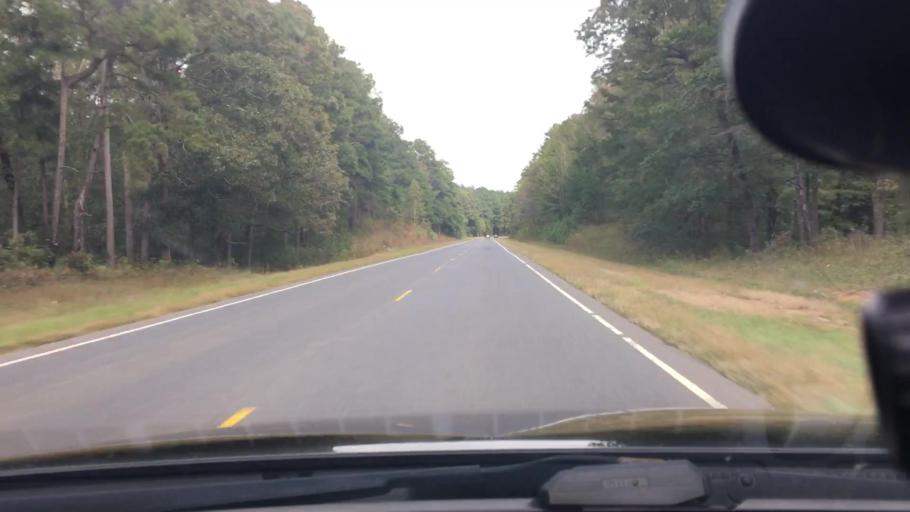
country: US
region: North Carolina
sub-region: Montgomery County
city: Troy
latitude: 35.3210
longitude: -79.9629
